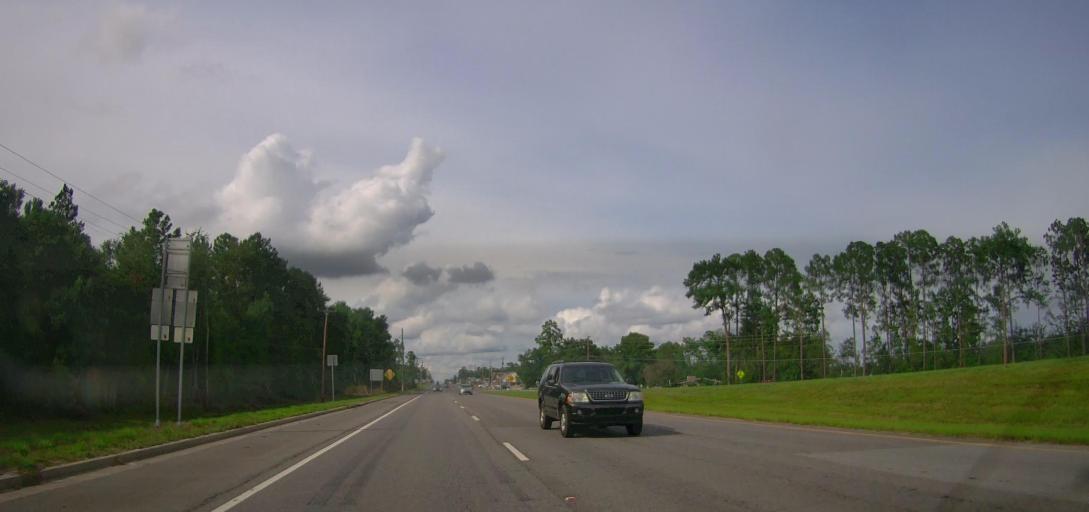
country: US
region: Georgia
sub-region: Wayne County
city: Jesup
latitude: 31.6250
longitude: -81.8677
